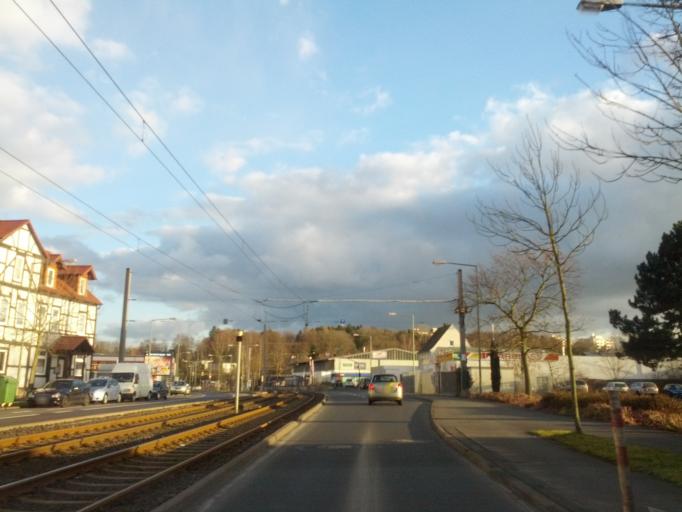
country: DE
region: Hesse
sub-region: Regierungsbezirk Kassel
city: Lohfelden
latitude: 51.2960
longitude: 9.5436
